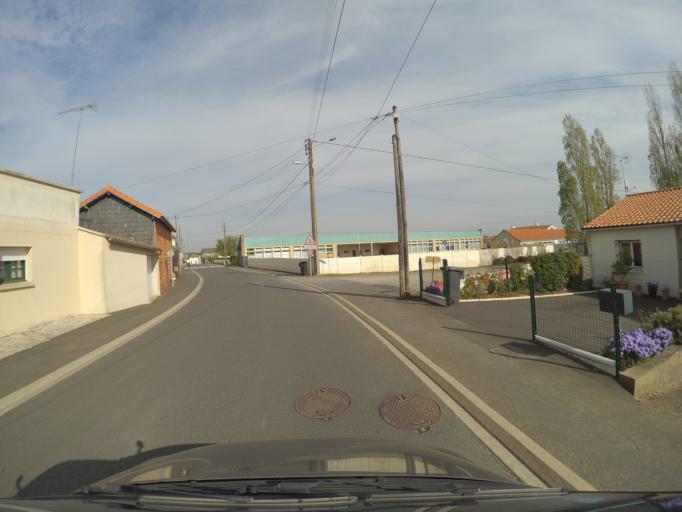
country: FR
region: Pays de la Loire
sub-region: Departement de Maine-et-Loire
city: Geste
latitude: 47.1801
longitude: -1.1138
